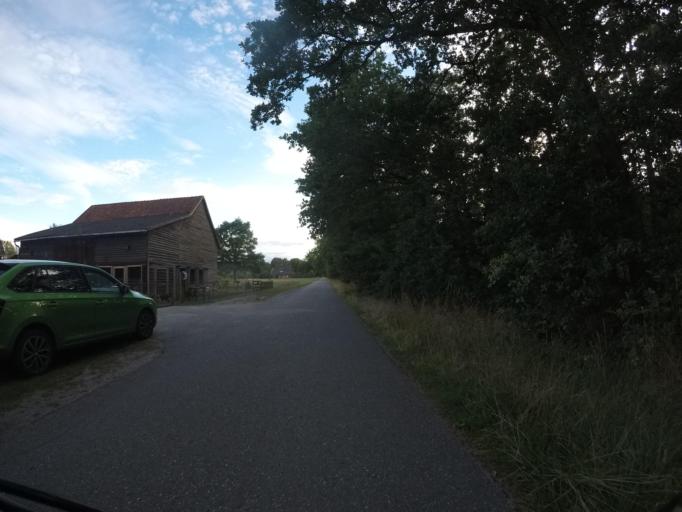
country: DE
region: Mecklenburg-Vorpommern
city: Lubtheen
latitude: 53.2398
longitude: 11.0394
